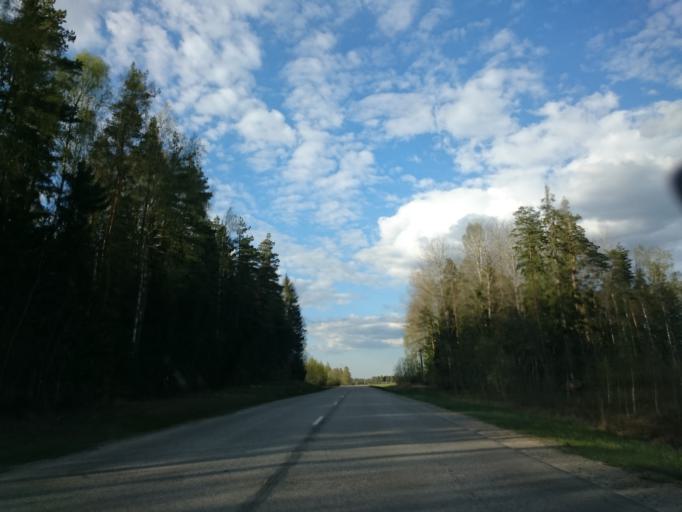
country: LV
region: Kuldigas Rajons
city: Kuldiga
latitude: 56.8897
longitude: 21.8835
